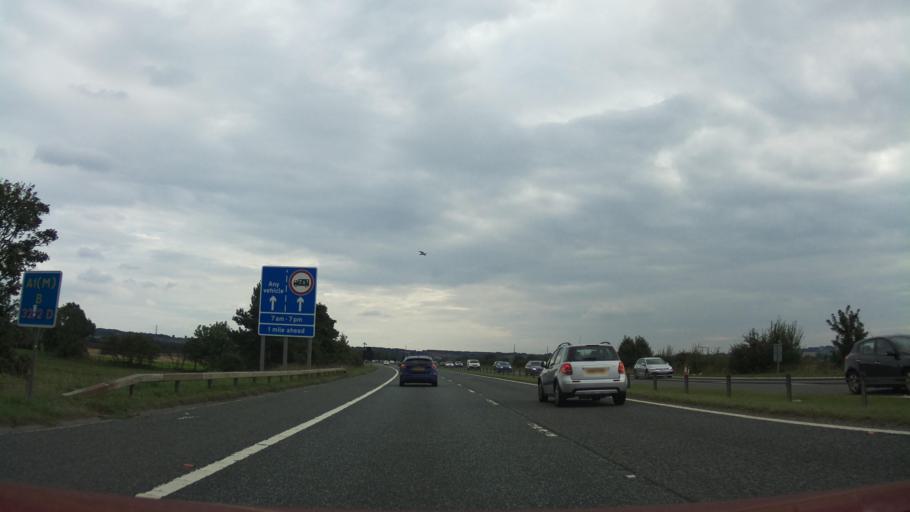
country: GB
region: England
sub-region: County Durham
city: Coxhoe
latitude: 54.7234
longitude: -1.5221
